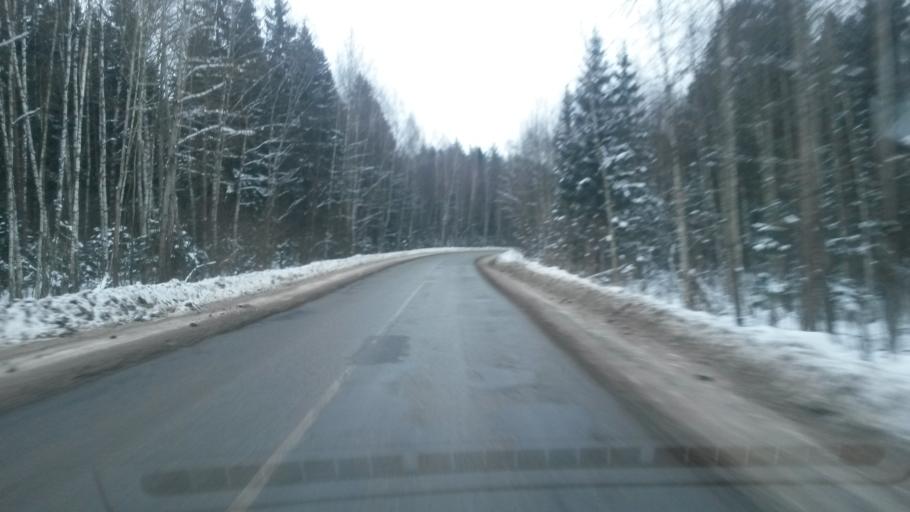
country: RU
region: Ivanovo
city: Kokhma
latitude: 56.9694
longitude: 41.0892
